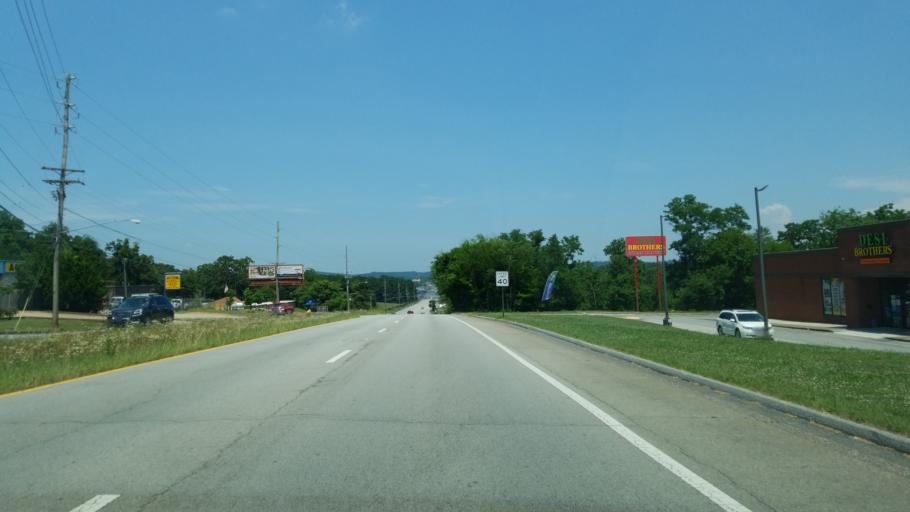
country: US
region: Tennessee
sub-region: Hamilton County
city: East Brainerd
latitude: 35.0347
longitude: -85.1784
